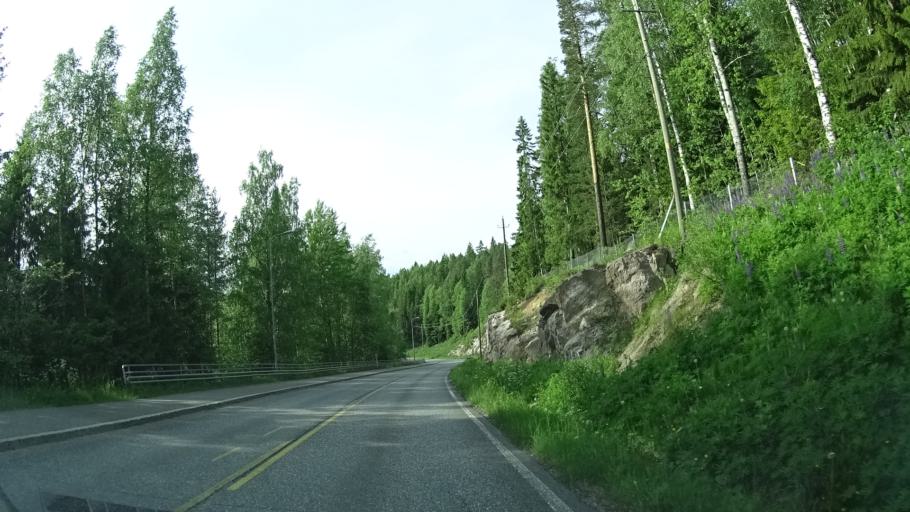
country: FI
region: Uusimaa
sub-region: Helsinki
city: Espoo
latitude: 60.2731
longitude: 24.5932
